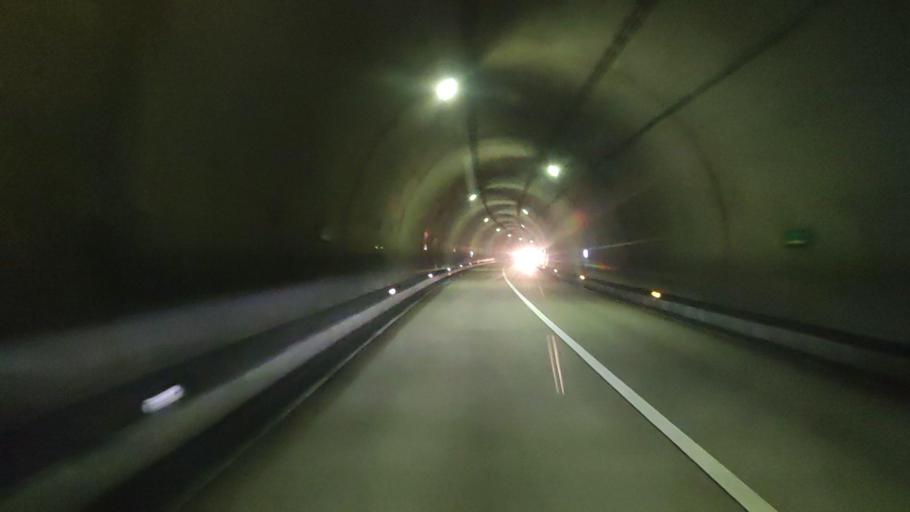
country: JP
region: Wakayama
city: Shingu
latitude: 33.8523
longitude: 135.8554
